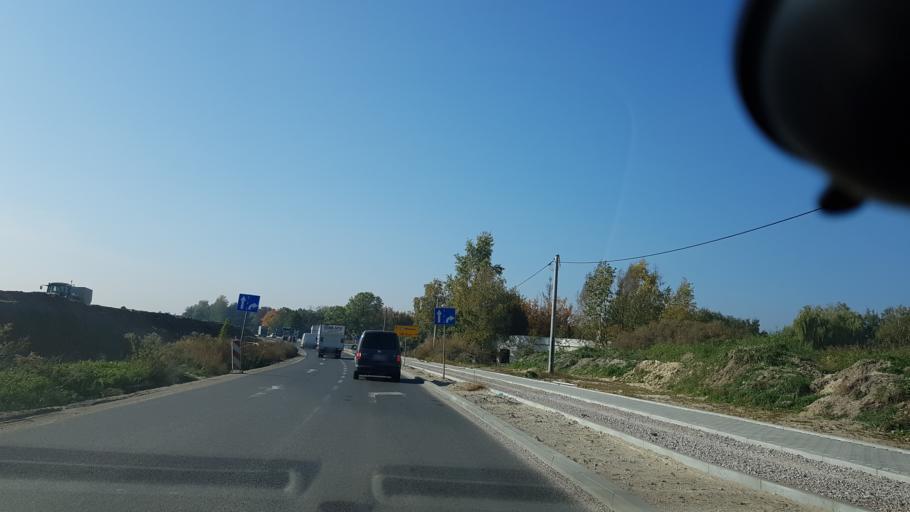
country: PL
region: Masovian Voivodeship
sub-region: Powiat pruszkowski
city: Nadarzyn
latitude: 52.0980
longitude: 20.8158
